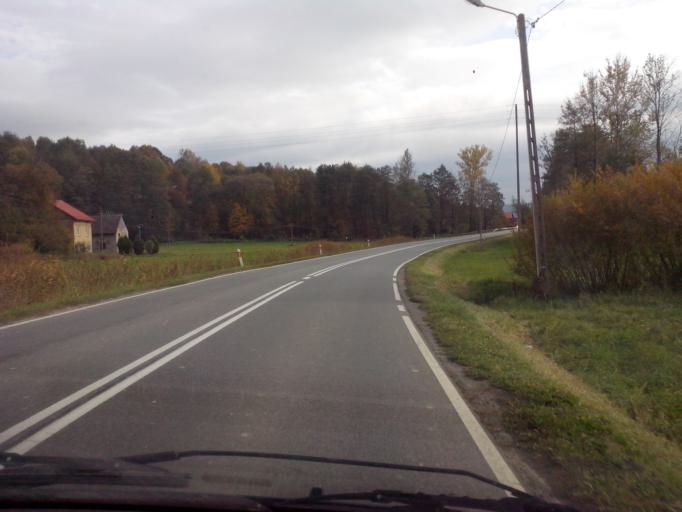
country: PL
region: Subcarpathian Voivodeship
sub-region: Powiat strzyzowski
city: Wisniowa
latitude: 49.8969
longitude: 21.6427
